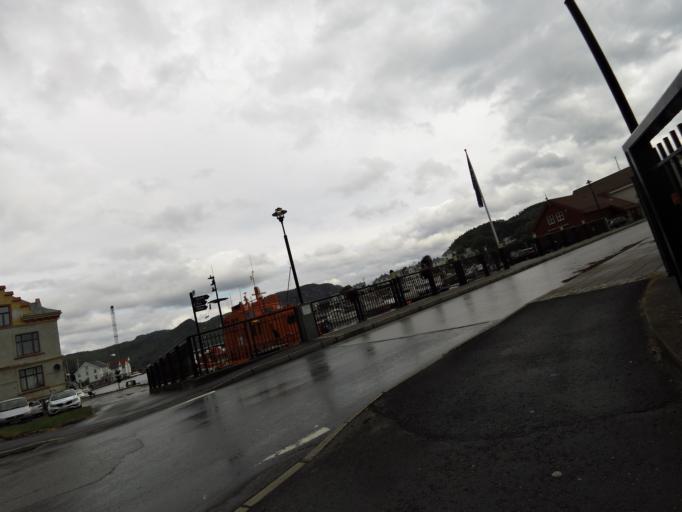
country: NO
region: Vest-Agder
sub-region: Farsund
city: Farsund
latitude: 58.0929
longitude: 6.8056
